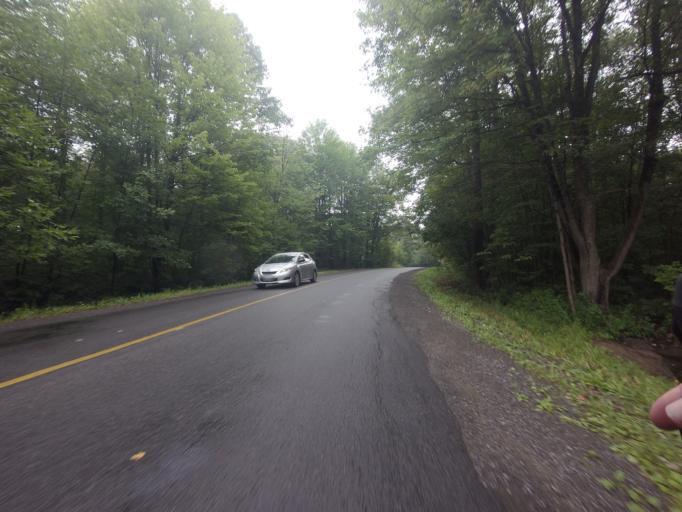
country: CA
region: Ontario
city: Bells Corners
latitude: 45.3409
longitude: -75.9801
